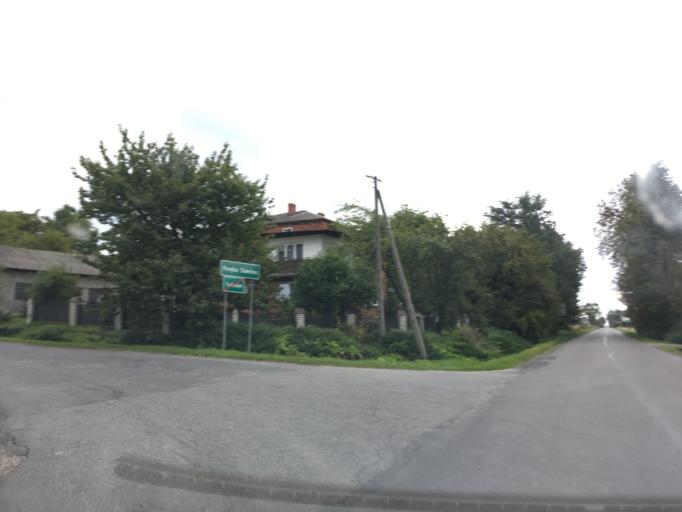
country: PL
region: Lesser Poland Voivodeship
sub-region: Powiat olkuski
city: Wolbrom
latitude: 50.4139
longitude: 19.7828
